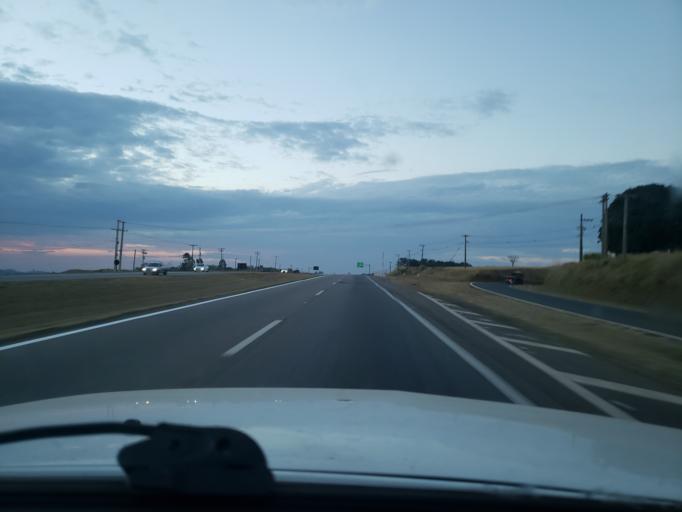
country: BR
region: Sao Paulo
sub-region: Mogi-Mirim
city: Mogi Mirim
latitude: -22.4785
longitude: -46.9813
